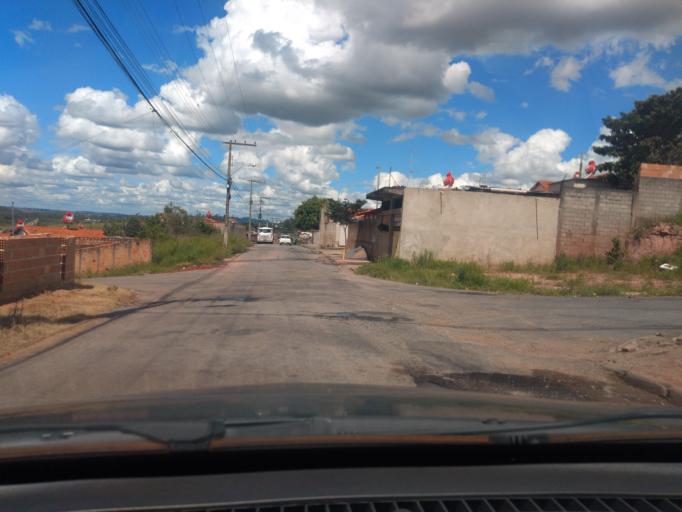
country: BR
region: Minas Gerais
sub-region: Tres Coracoes
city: Tres Coracoes
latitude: -21.6834
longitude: -45.2490
